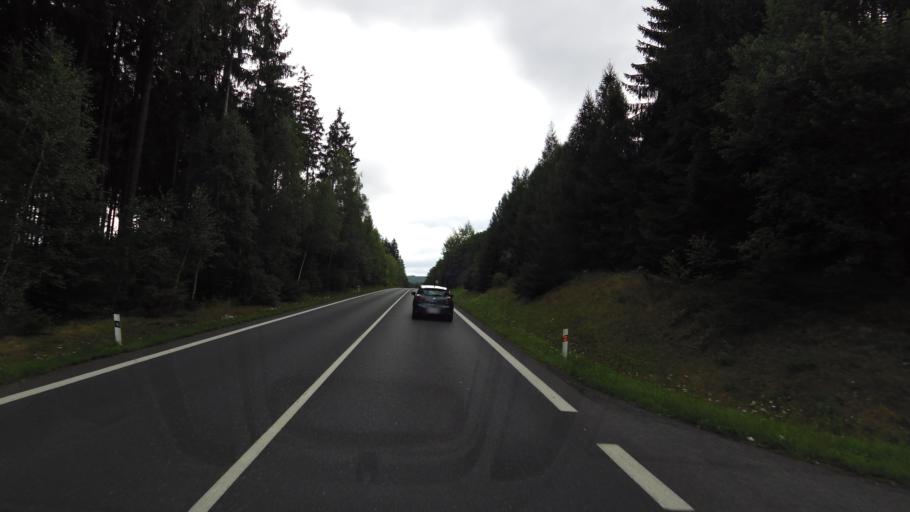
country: DE
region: Bavaria
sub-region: Upper Palatinate
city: Furth im Wald
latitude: 49.3745
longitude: 12.8524
